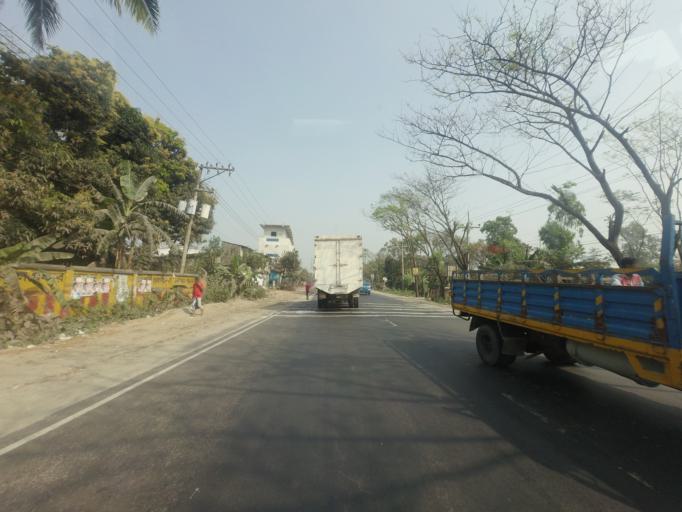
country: BD
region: Dhaka
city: Narsingdi
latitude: 23.8791
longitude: 90.6668
